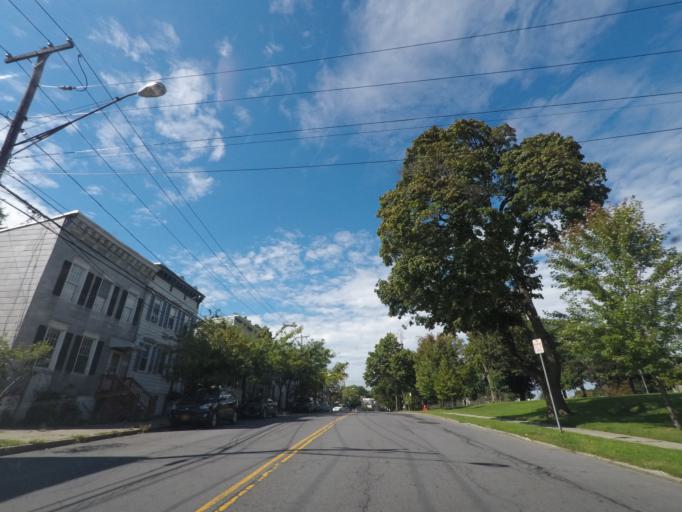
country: US
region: New York
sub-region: Albany County
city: Albany
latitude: 42.6449
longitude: -73.7691
